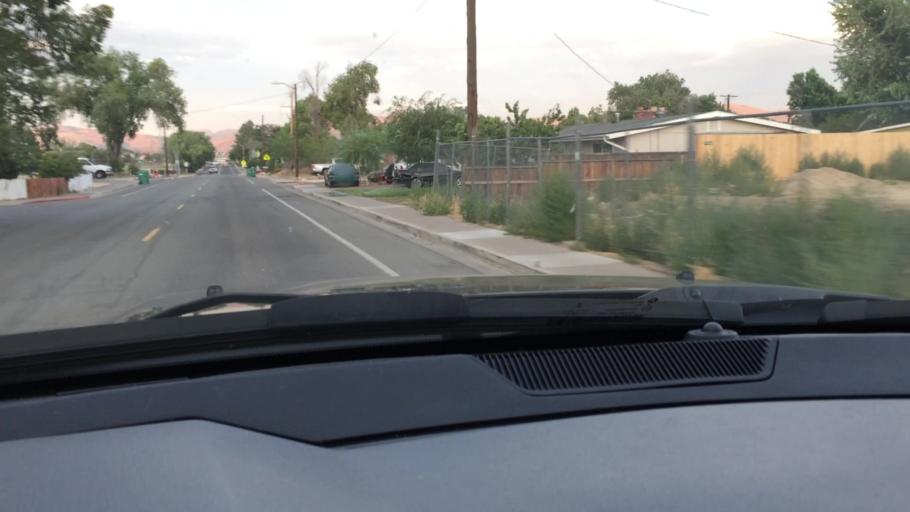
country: US
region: Nevada
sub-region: Washoe County
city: Reno
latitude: 39.5129
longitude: -119.7960
